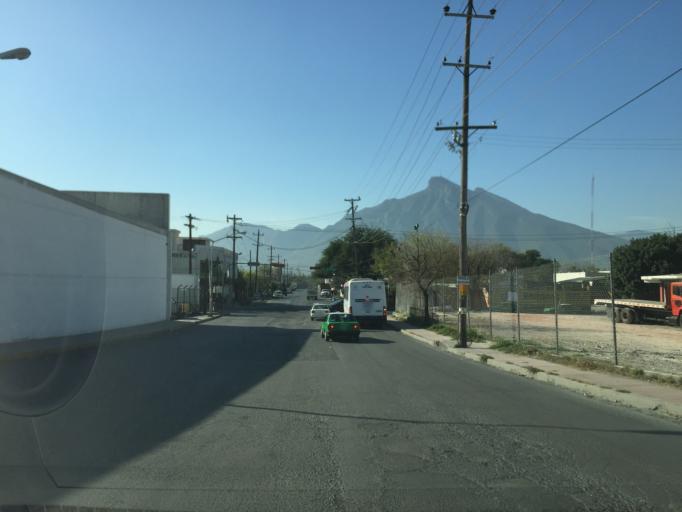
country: MX
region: Nuevo Leon
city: Guadalupe
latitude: 25.6957
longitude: -100.2172
